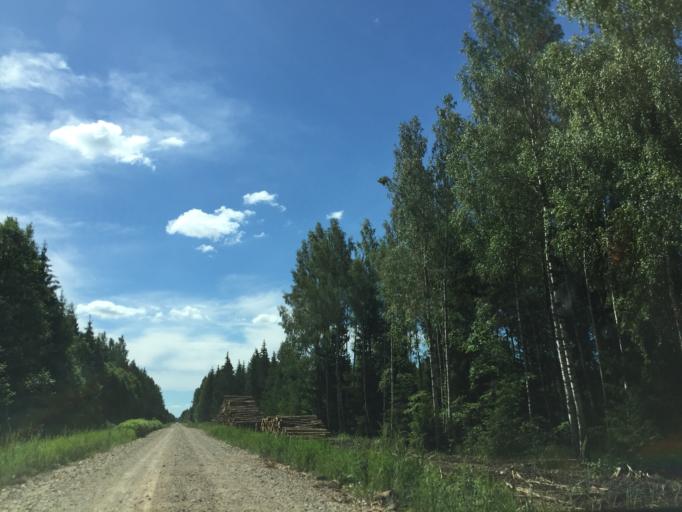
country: LV
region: Ventspils Rajons
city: Piltene
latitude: 57.2798
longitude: 21.8313
